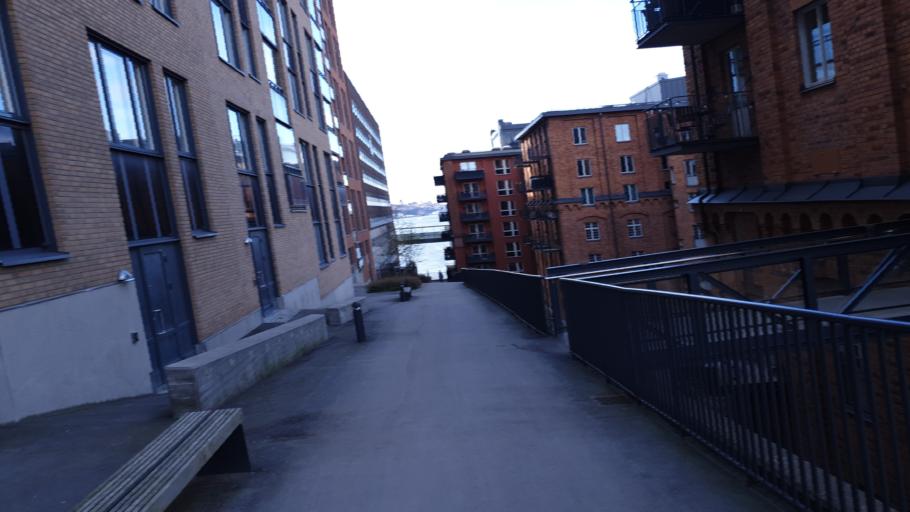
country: SE
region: Stockholm
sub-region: Nacka Kommun
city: Nacka
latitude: 59.3173
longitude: 18.1398
